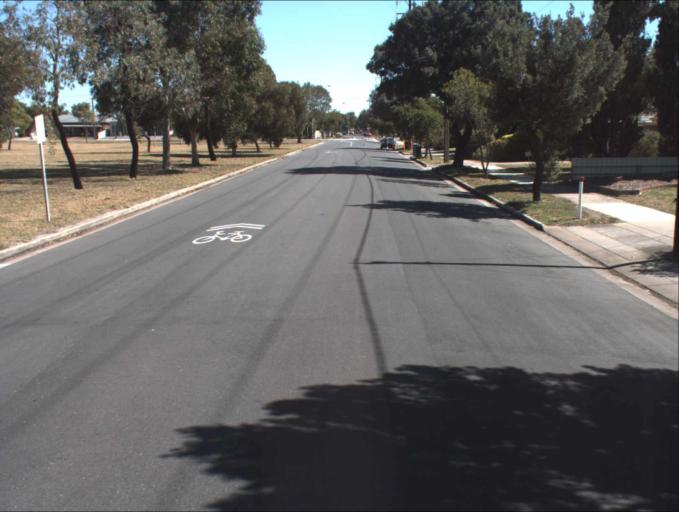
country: AU
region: South Australia
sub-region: Port Adelaide Enfield
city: Birkenhead
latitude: -34.8173
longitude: 138.4994
